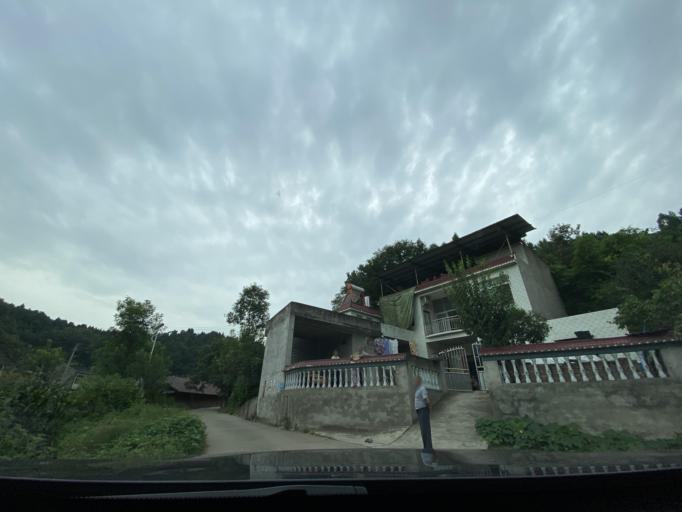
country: CN
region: Sichuan
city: Jiancheng
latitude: 30.3869
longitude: 104.4857
